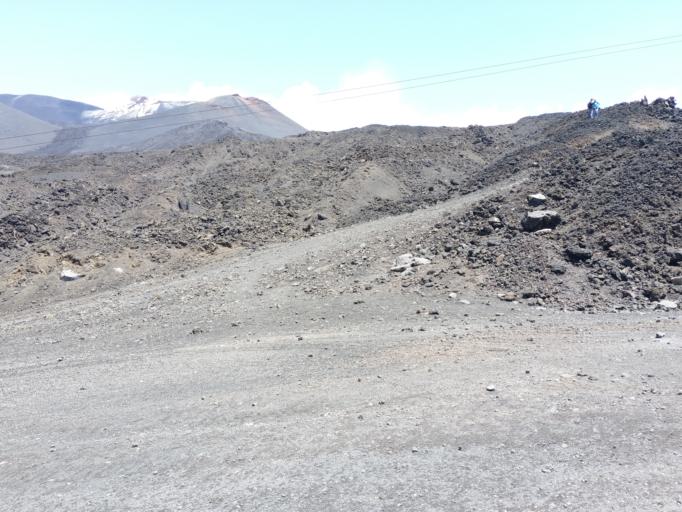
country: IT
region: Sicily
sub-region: Catania
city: Ragalna
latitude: 37.7184
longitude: 14.9983
